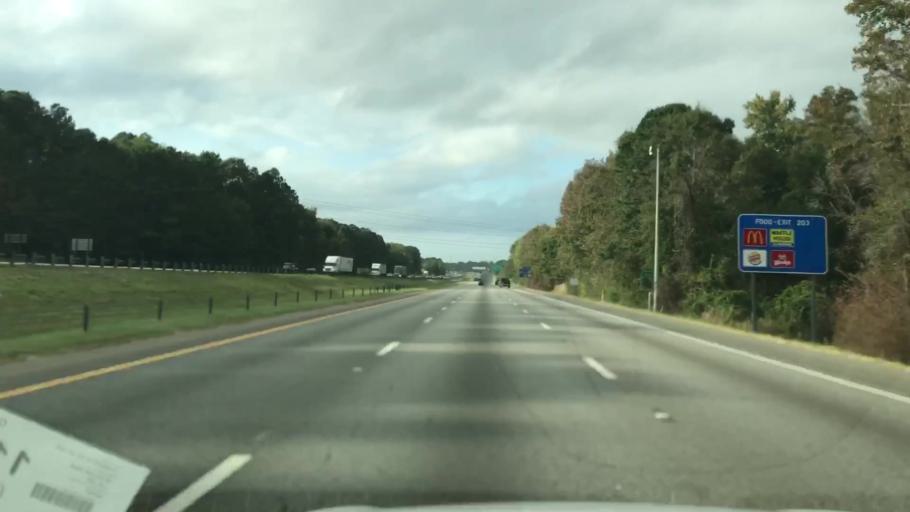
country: US
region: South Carolina
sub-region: Berkeley County
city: Ladson
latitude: 32.9918
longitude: -80.0865
